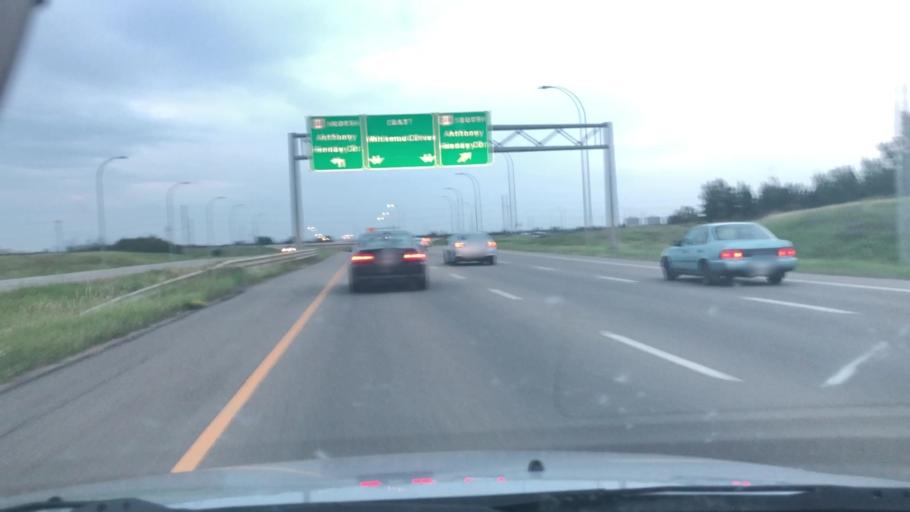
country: CA
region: Alberta
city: St. Albert
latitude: 53.5122
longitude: -113.6684
